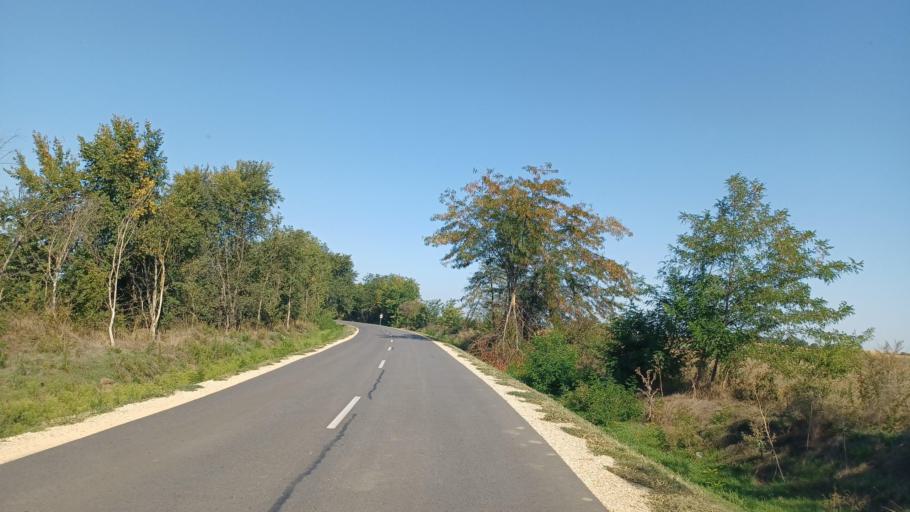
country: HU
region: Tolna
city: Nemetker
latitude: 46.6958
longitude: 18.7945
